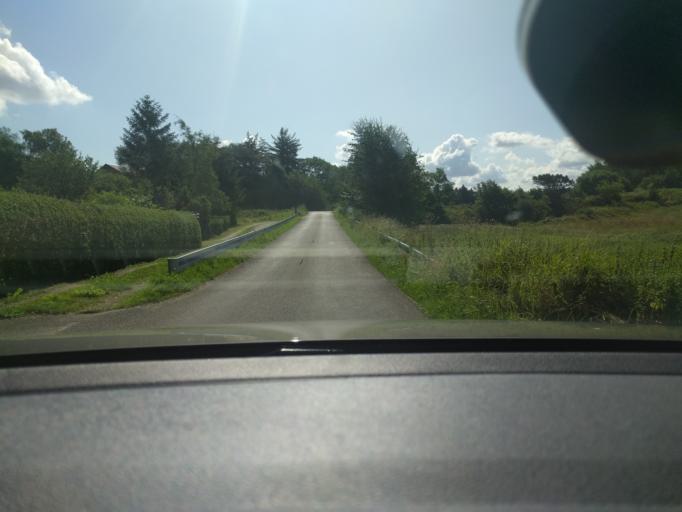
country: DK
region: Central Jutland
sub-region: Viborg Kommune
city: Bjerringbro
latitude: 56.5024
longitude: 9.5841
